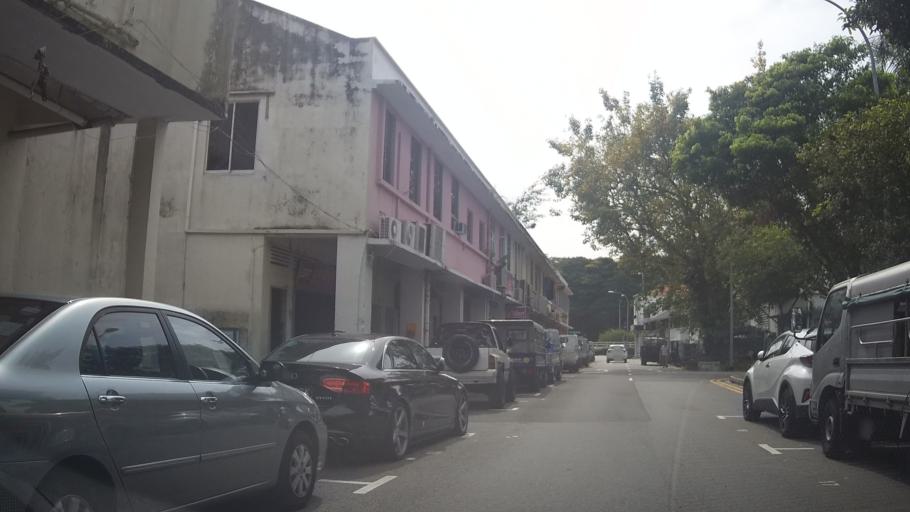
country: SG
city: Singapore
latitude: 1.3274
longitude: 103.8663
